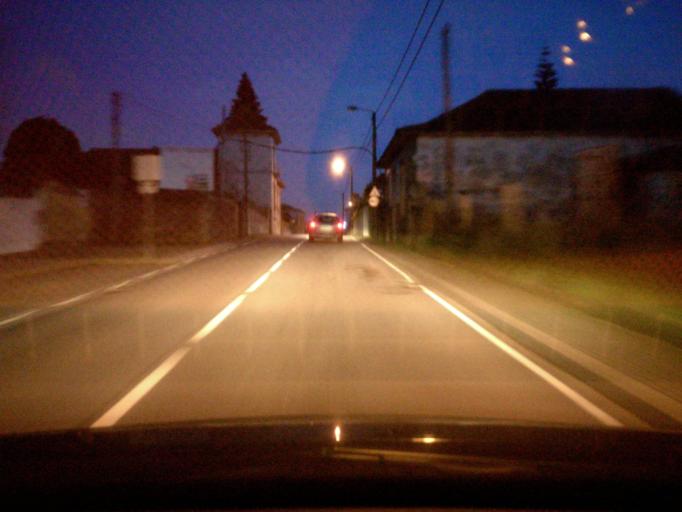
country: PT
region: Porto
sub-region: Maia
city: Gemunde
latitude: 41.2467
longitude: -8.6396
